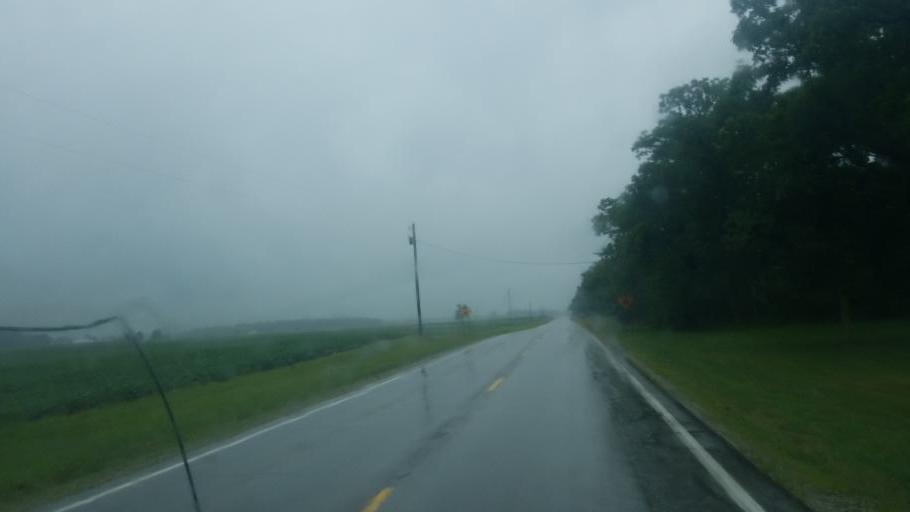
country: US
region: Indiana
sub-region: Huntington County
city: Warren
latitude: 40.6546
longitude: -85.3662
